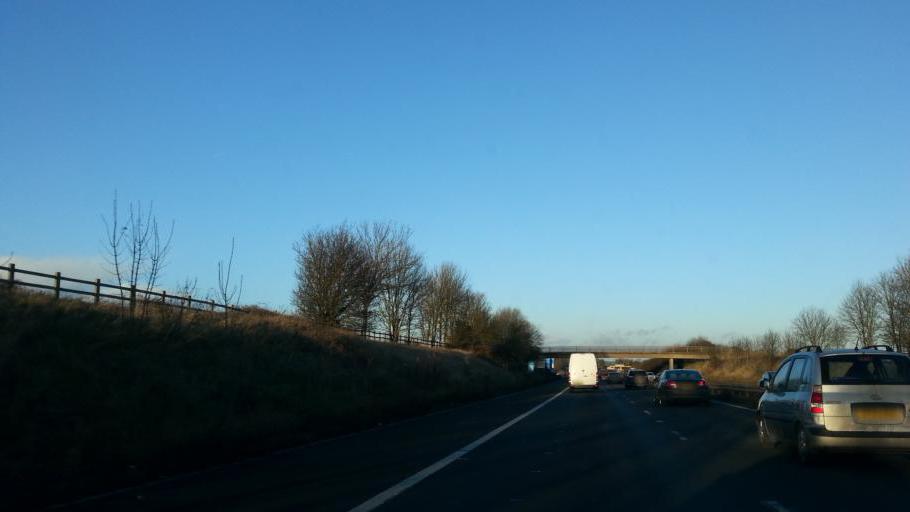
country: GB
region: England
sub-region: Derbyshire
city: Netherseal
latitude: 52.6809
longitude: -1.5528
